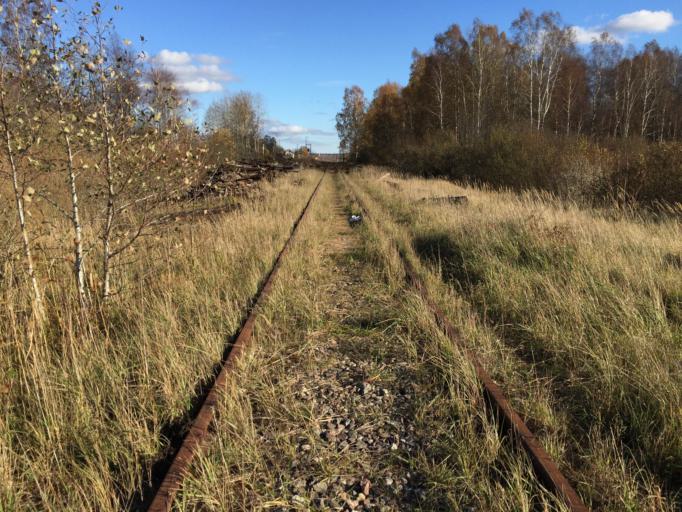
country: LV
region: Tukuma Rajons
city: Tukums
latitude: 56.9601
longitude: 23.1025
